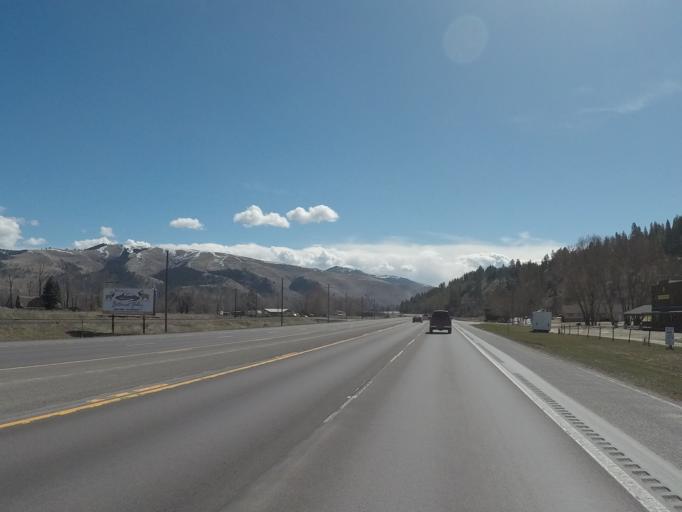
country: US
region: Montana
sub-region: Missoula County
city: Lolo
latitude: 46.7776
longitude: -114.0892
